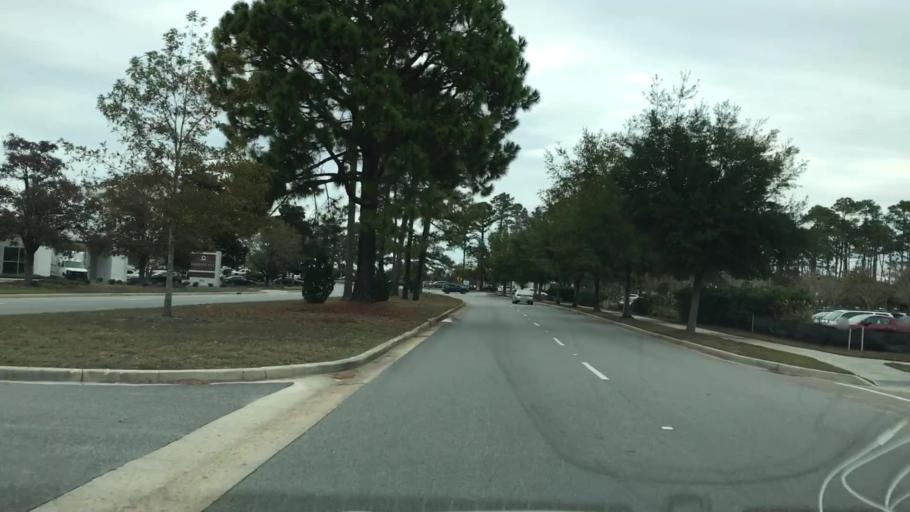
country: US
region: South Carolina
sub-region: Horry County
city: Myrtle Beach
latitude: 33.7590
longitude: -78.8163
